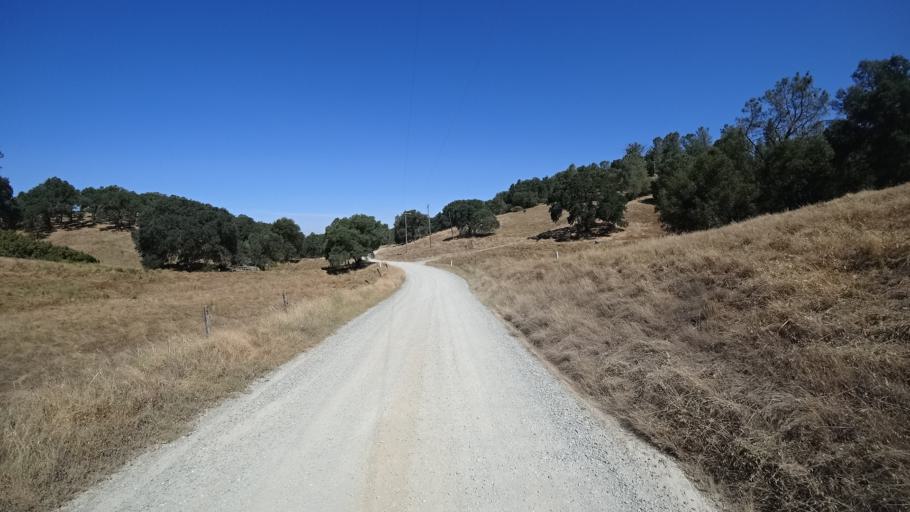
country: US
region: California
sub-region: Calaveras County
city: Valley Springs
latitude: 38.2199
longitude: -120.8784
